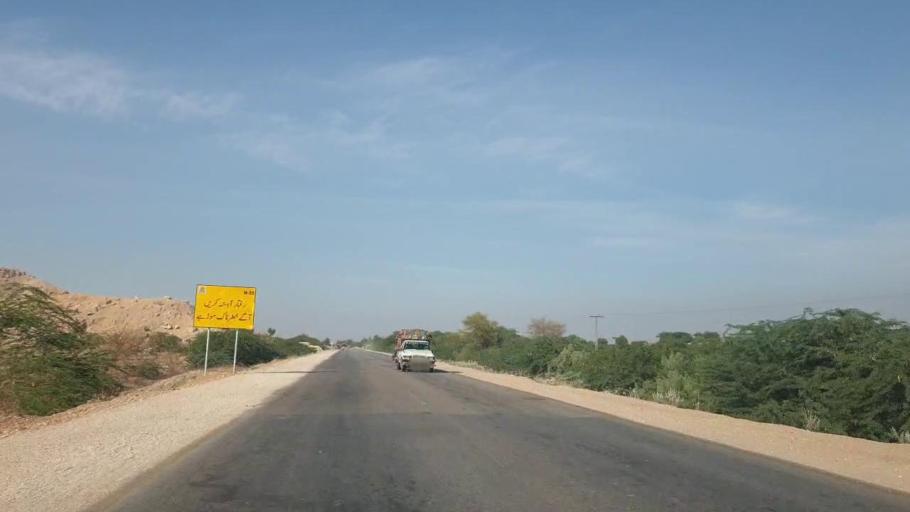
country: PK
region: Sindh
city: Sehwan
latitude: 26.3085
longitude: 67.8927
